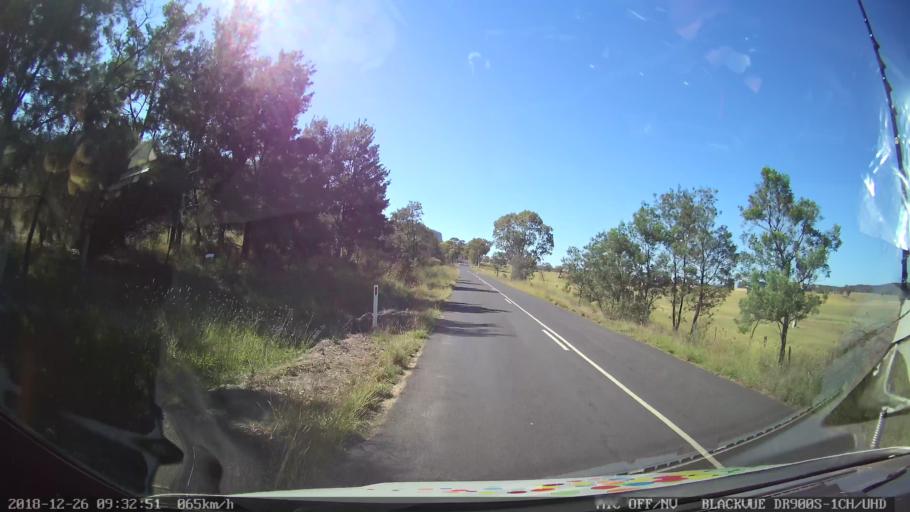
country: AU
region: New South Wales
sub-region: Mid-Western Regional
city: Kandos
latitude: -32.8888
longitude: 150.0331
